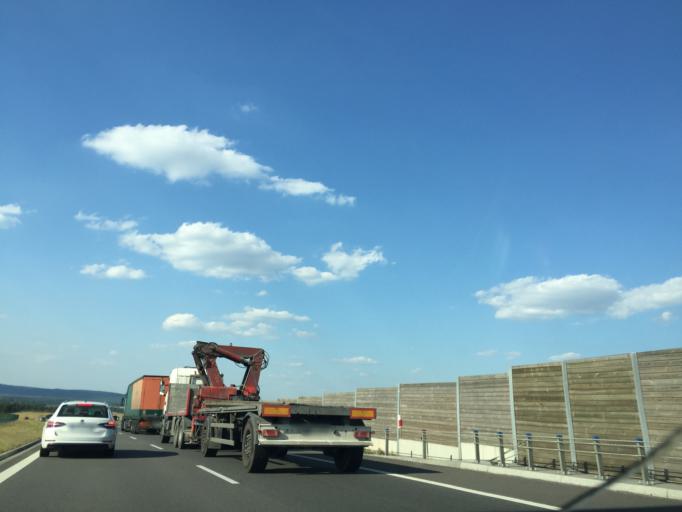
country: PL
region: Swietokrzyskie
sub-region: Powiat jedrzejowski
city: Sobkow
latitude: 50.7188
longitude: 20.4096
